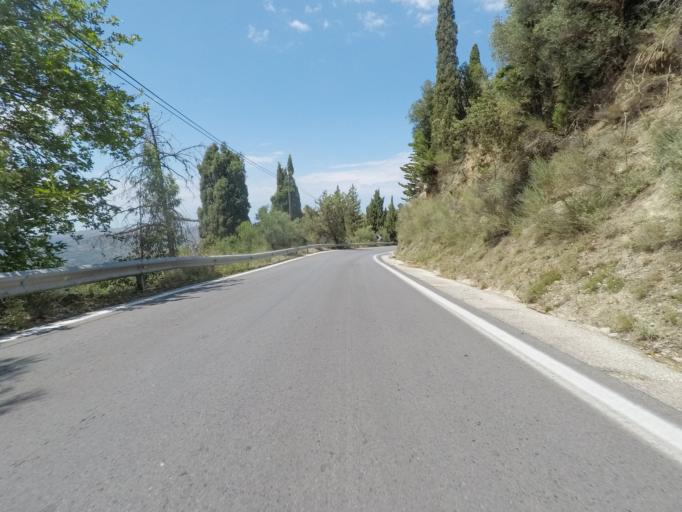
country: GR
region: Crete
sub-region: Nomos Irakleiou
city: Mokhos
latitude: 35.2231
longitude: 25.4621
